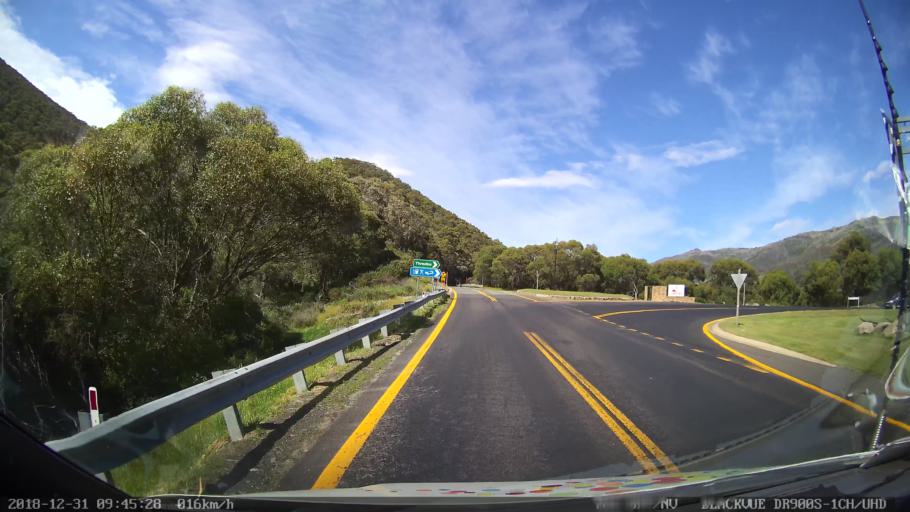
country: AU
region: New South Wales
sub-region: Snowy River
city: Jindabyne
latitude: -36.4999
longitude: 148.3170
